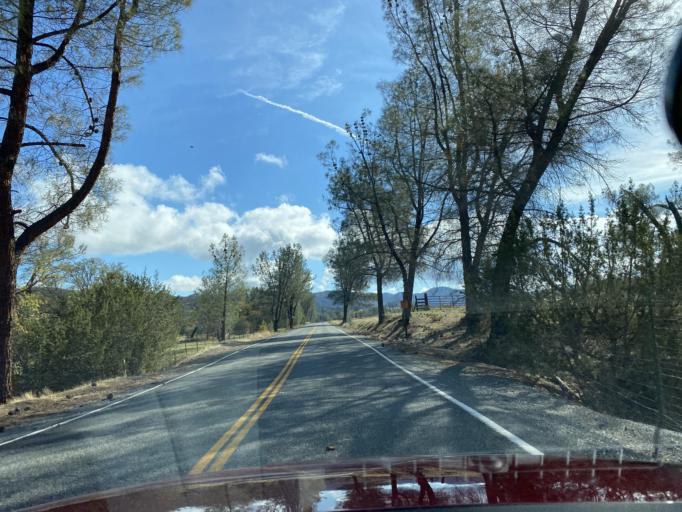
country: US
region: California
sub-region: Glenn County
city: Willows
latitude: 39.4424
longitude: -122.5119
